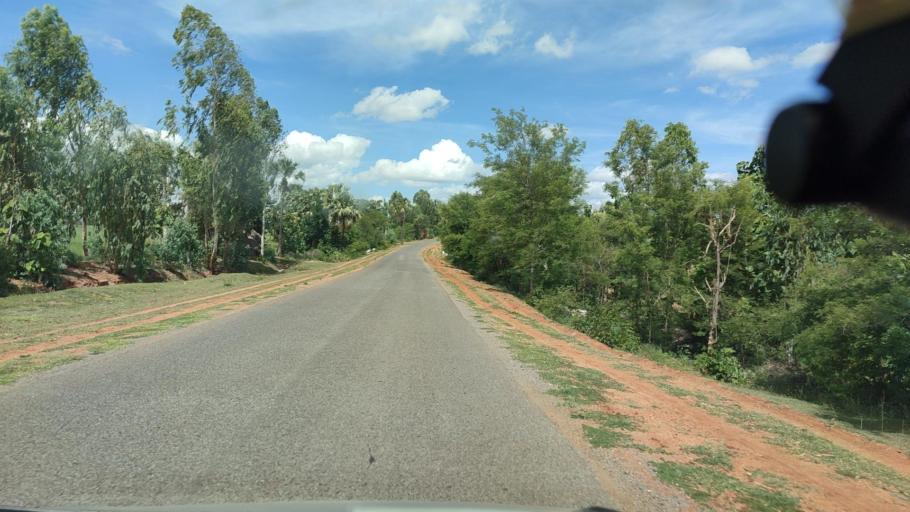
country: MM
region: Magway
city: Magway
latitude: 20.1925
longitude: 95.1573
